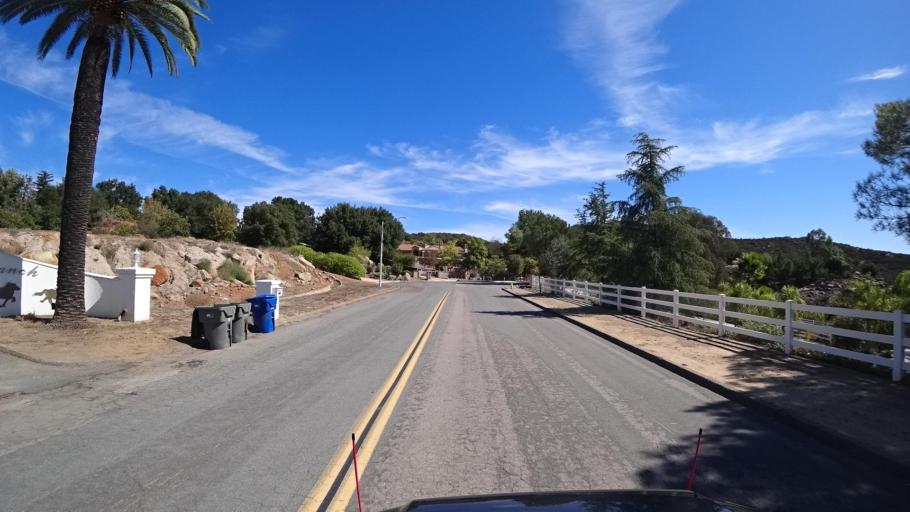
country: US
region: California
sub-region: San Diego County
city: Harbison Canyon
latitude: 32.8768
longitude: -116.8258
